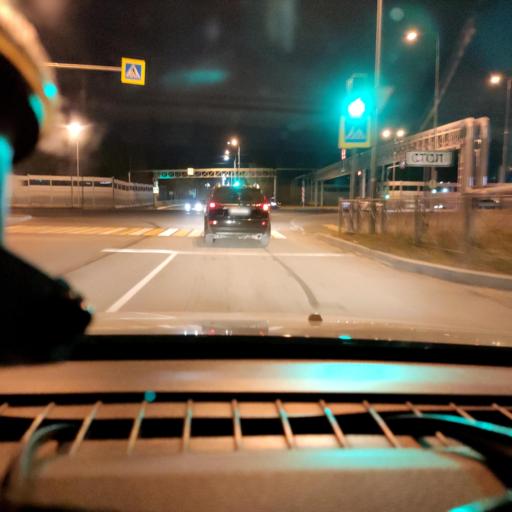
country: RU
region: Samara
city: Bereza
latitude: 53.5121
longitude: 50.1438
